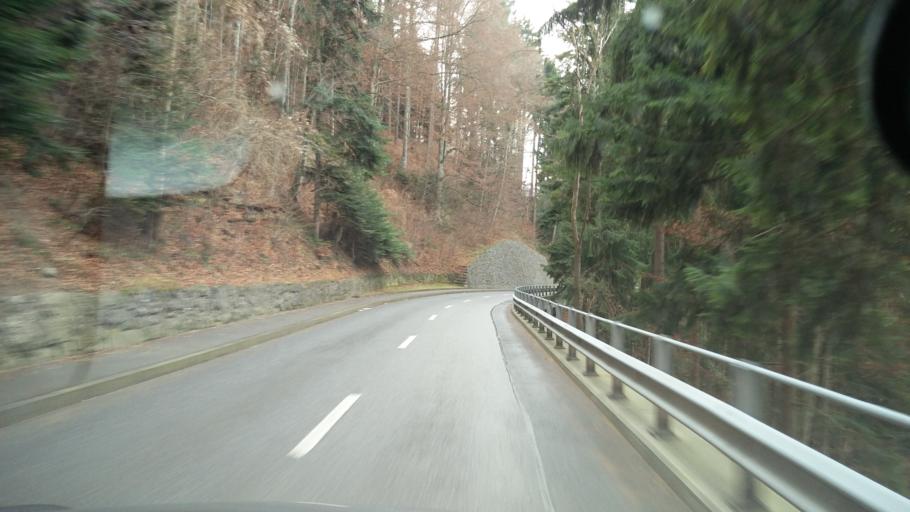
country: LI
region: Planken
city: Planken
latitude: 47.1816
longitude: 9.5404
